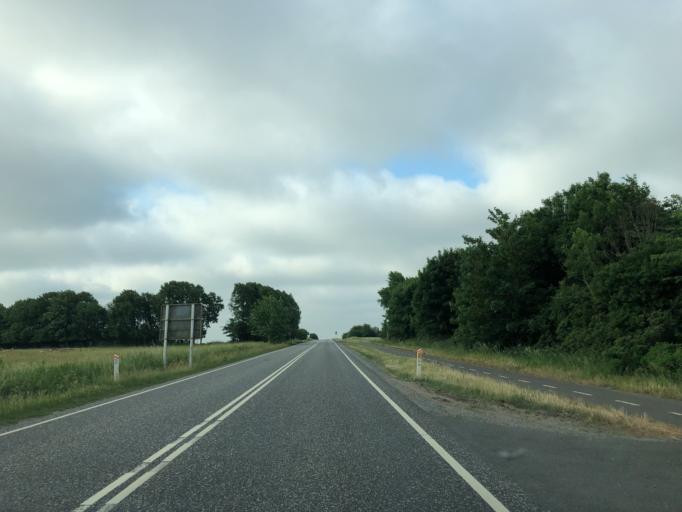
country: DK
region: South Denmark
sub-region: Vejle Kommune
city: Give
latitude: 55.8373
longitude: 9.2517
